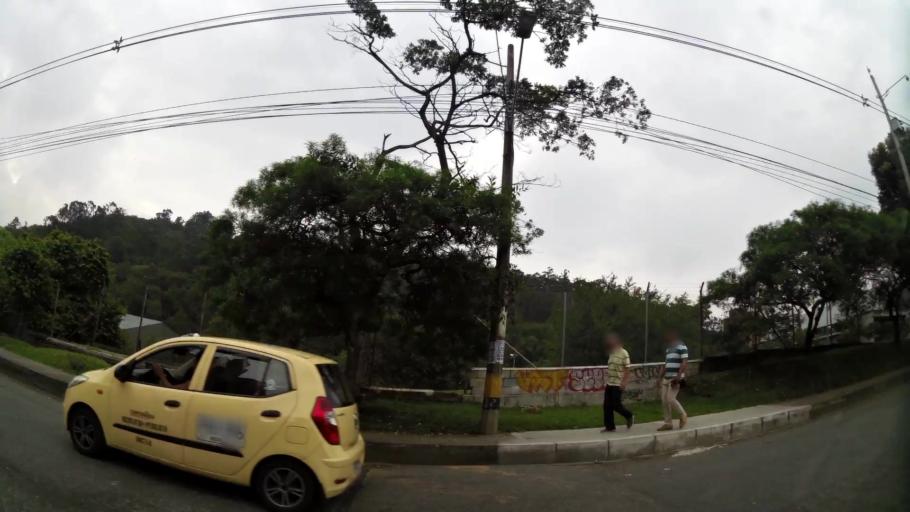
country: CO
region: Antioquia
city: Medellin
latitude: 6.2659
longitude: -75.5876
